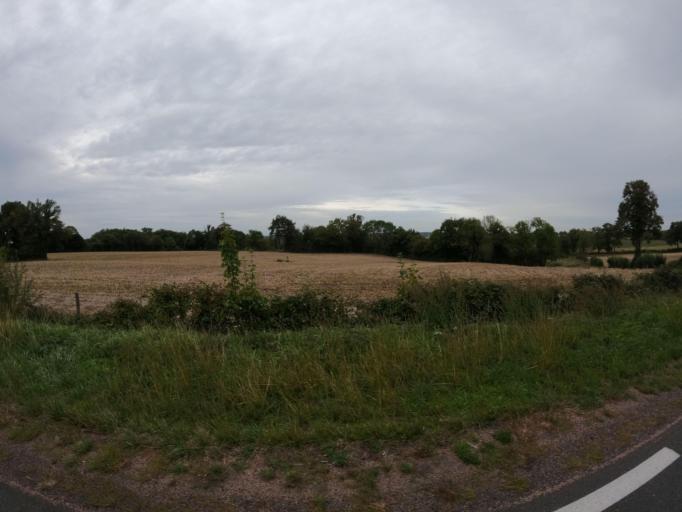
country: FR
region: Limousin
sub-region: Departement de la Haute-Vienne
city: Chateauponsac
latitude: 46.1925
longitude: 1.2592
